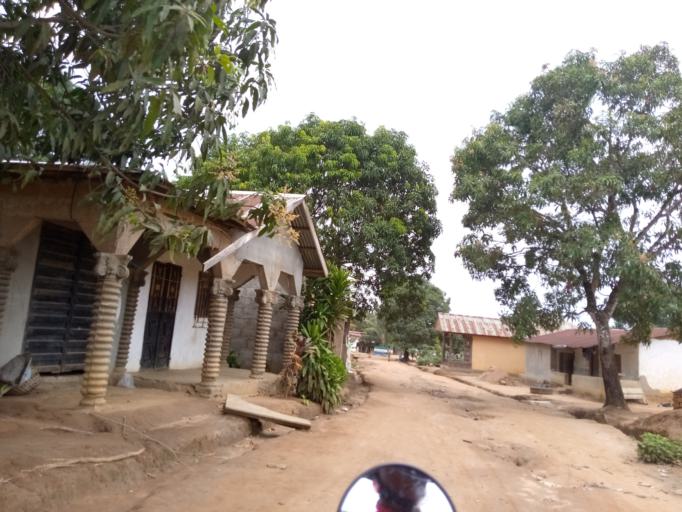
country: SL
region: Western Area
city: Waterloo
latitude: 8.3337
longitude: -13.0219
